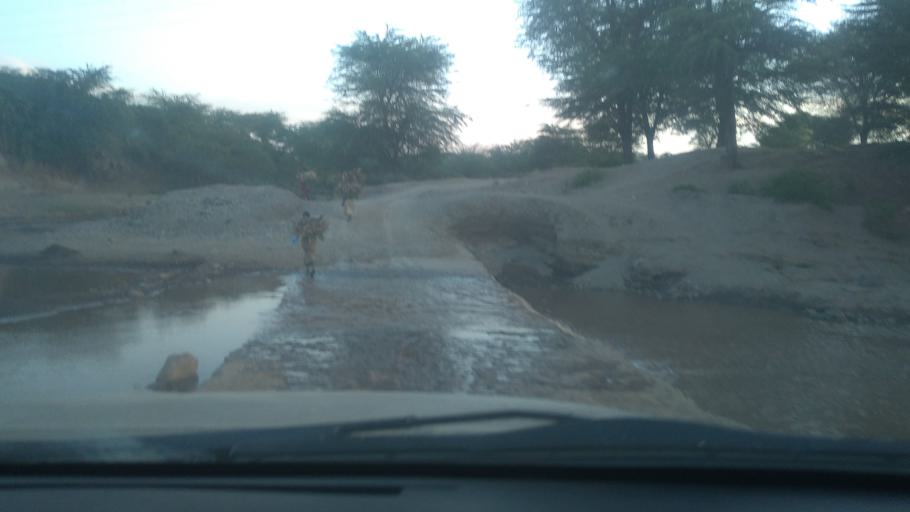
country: ET
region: Oromiya
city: Asbe Teferi
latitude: 9.2397
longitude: 40.7669
